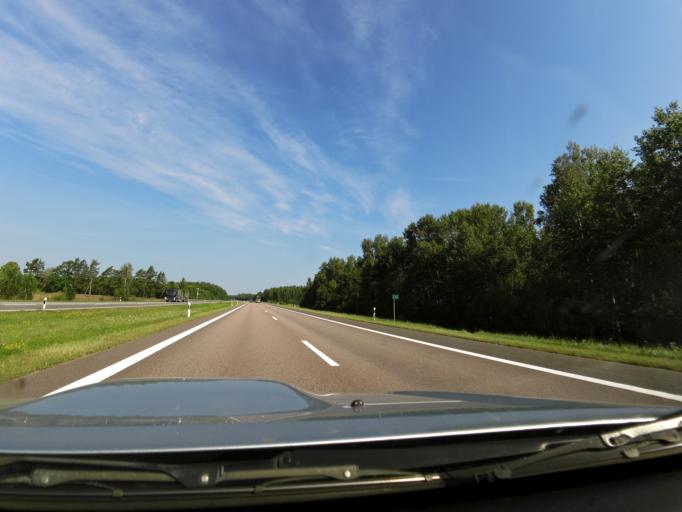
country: LT
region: Panevezys
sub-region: Panevezys City
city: Panevezys
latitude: 55.6407
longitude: 24.3962
